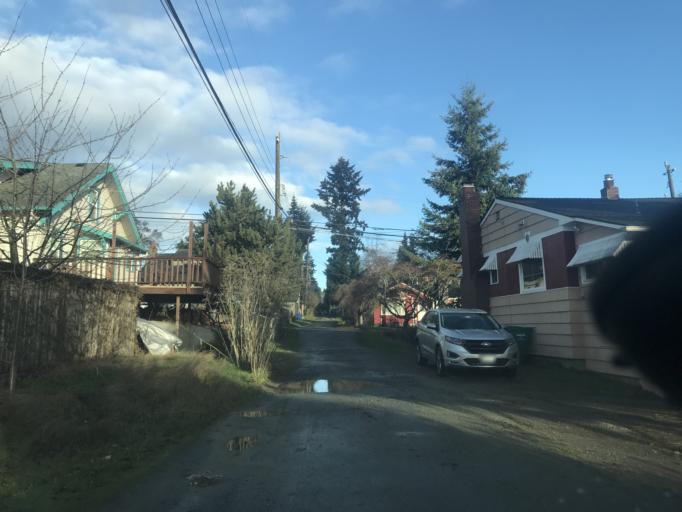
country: US
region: Washington
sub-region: King County
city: White Center
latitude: 47.5243
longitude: -122.3733
